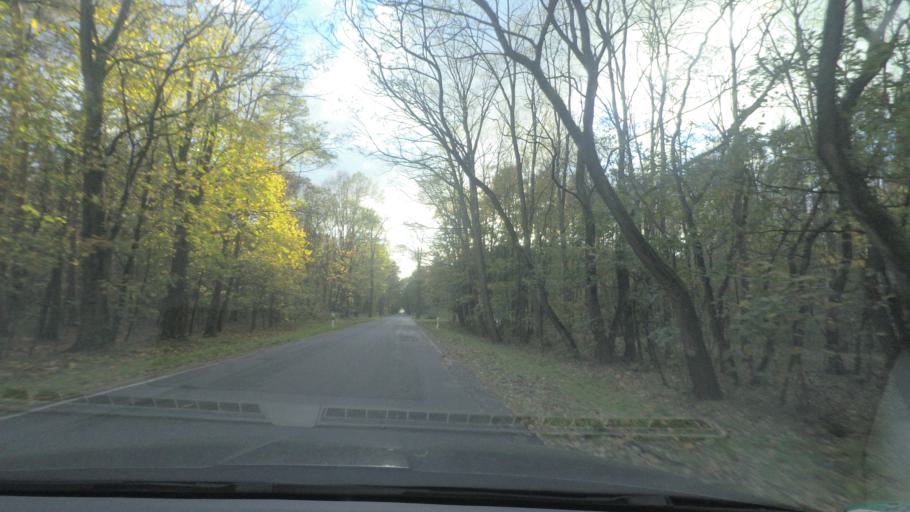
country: DE
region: Brandenburg
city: Ihlow
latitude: 51.9685
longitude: 13.3409
